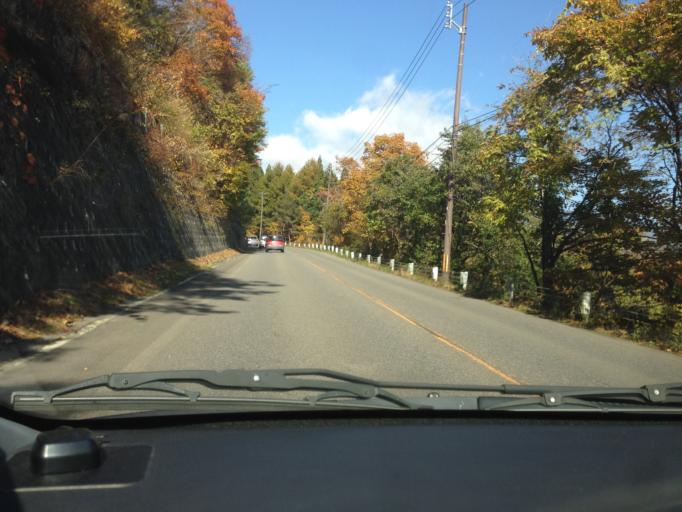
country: JP
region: Fukushima
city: Inawashiro
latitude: 37.6353
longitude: 140.1034
